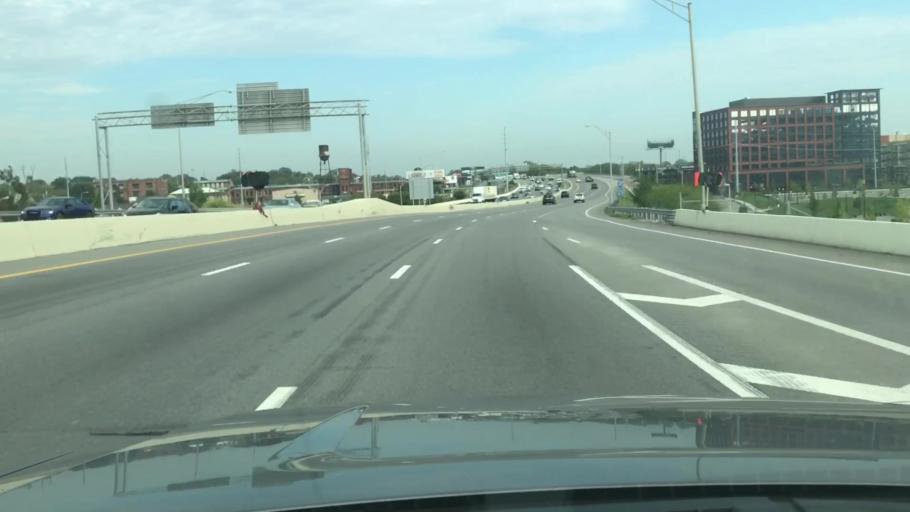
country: US
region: Tennessee
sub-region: Davidson County
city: Nashville
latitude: 36.1609
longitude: -86.7908
